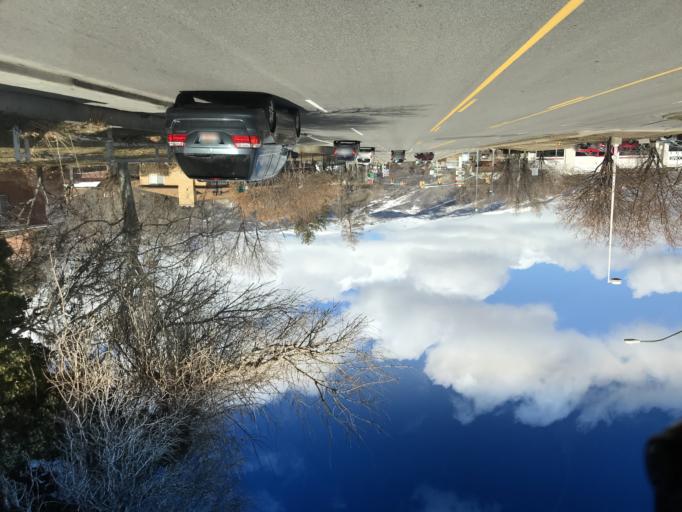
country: US
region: Utah
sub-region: Davis County
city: Woods Cross
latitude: 40.8651
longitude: -111.8797
